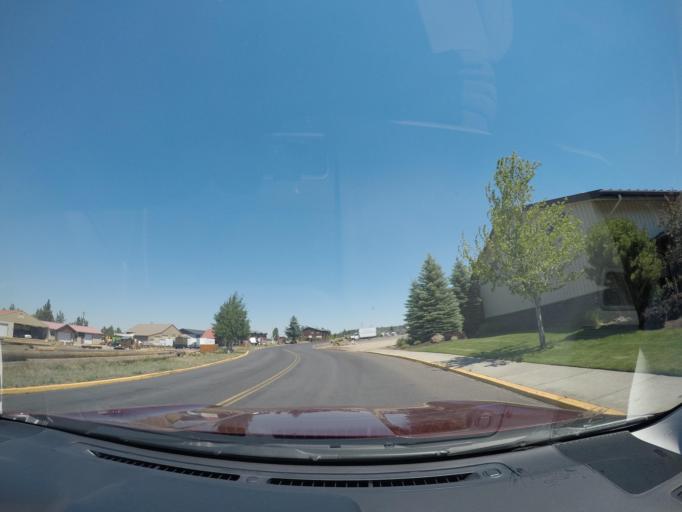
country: US
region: Oregon
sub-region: Deschutes County
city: Sisters
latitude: 44.2977
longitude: -121.5507
